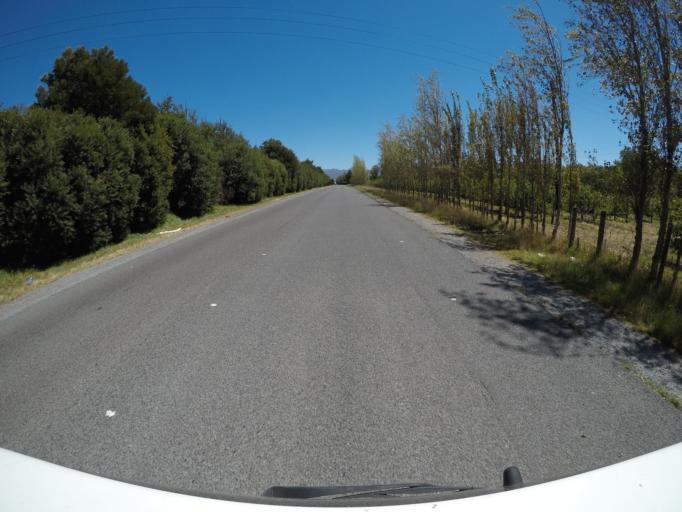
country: ZA
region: Western Cape
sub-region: Overberg District Municipality
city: Grabouw
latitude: -34.1845
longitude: 19.0384
